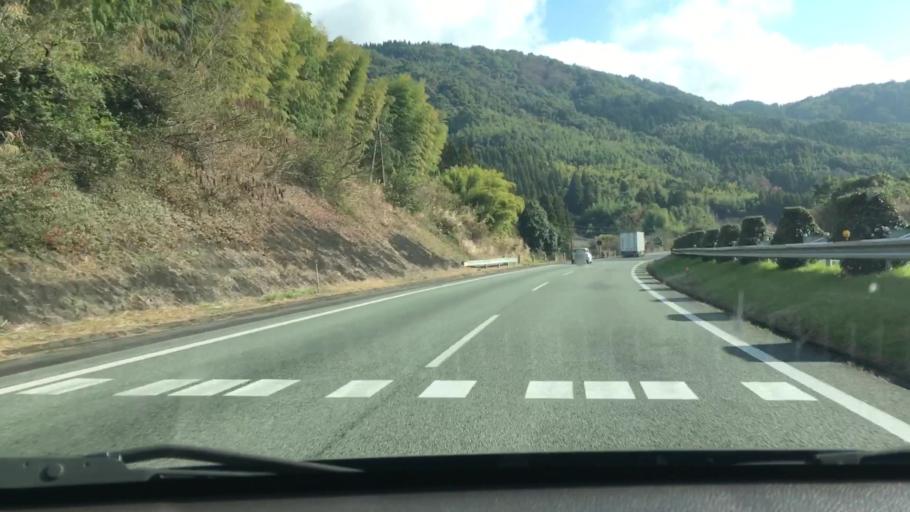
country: JP
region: Kumamoto
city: Matsubase
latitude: 32.6155
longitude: 130.7226
